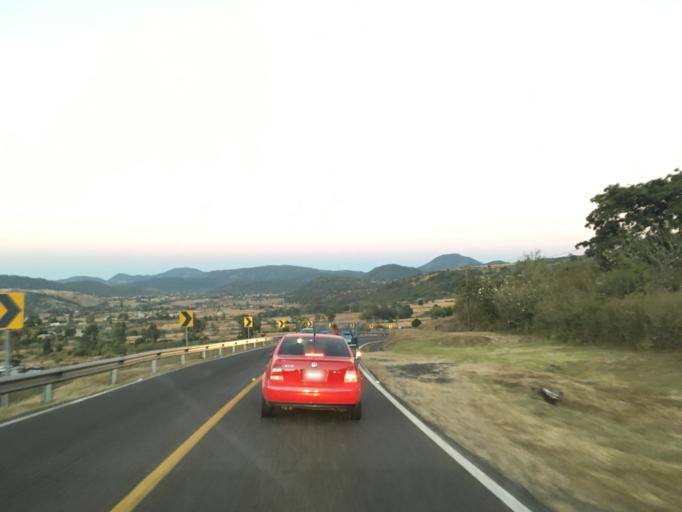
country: MX
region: Michoacan
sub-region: Zinapecuaro
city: Santa Clara del Tule
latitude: 19.8138
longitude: -100.8233
